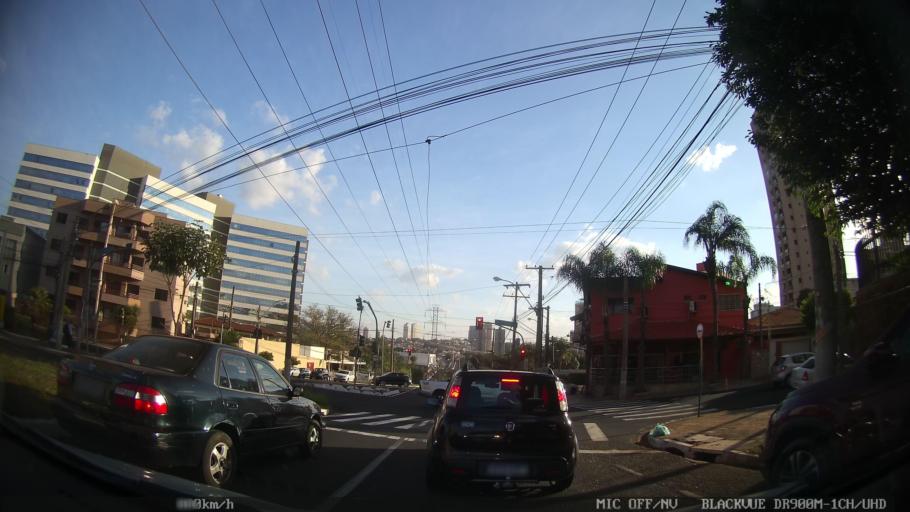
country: BR
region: Sao Paulo
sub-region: Ribeirao Preto
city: Ribeirao Preto
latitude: -21.1890
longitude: -47.7921
